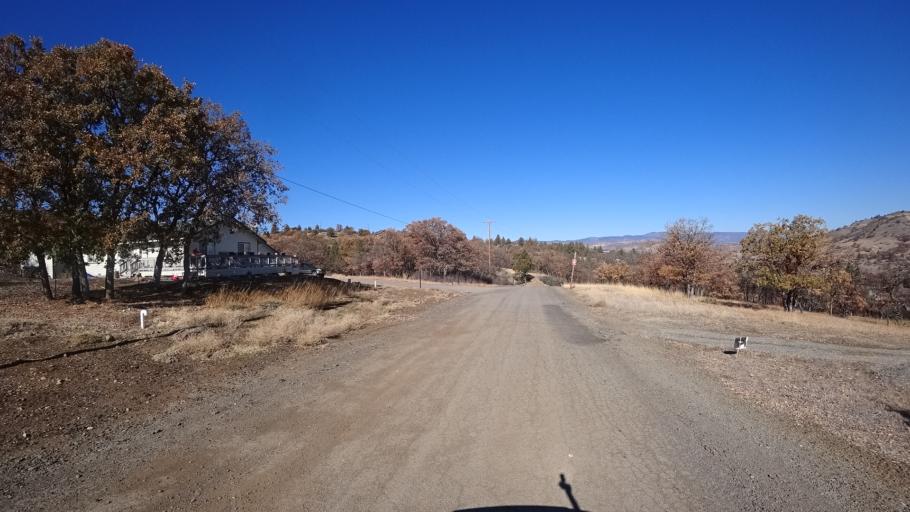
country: US
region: California
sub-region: Siskiyou County
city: Montague
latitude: 41.8737
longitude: -122.4803
